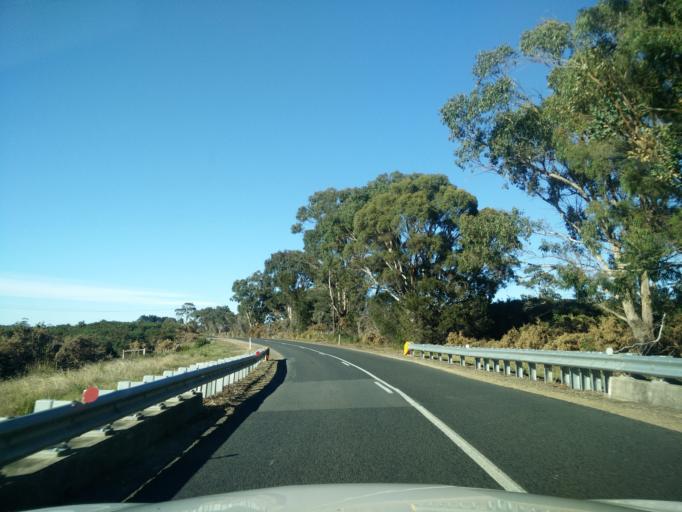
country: AU
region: Tasmania
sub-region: Break O'Day
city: St Helens
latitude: -41.9277
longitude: 148.2299
